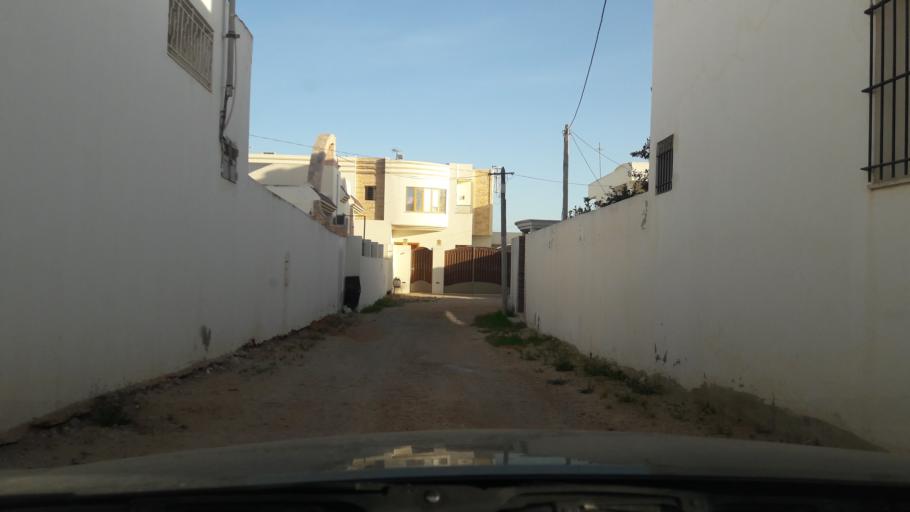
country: TN
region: Safaqis
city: Al Qarmadah
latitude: 34.7953
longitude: 10.7592
